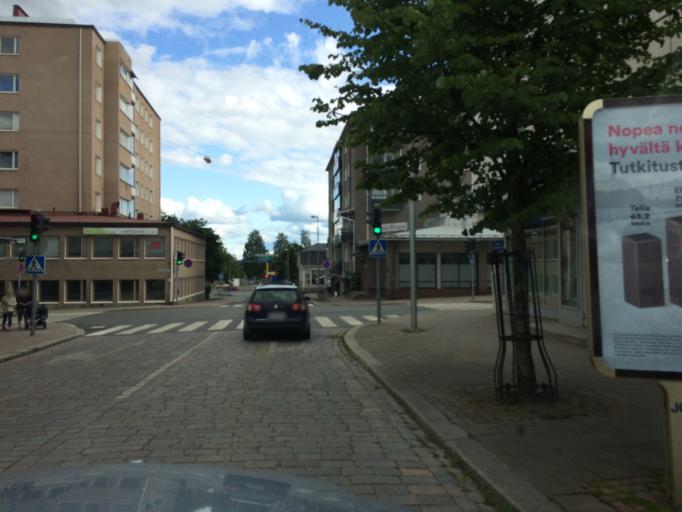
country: FI
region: Haeme
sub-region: Haemeenlinna
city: Haemeenlinna
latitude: 60.9949
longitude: 24.4626
